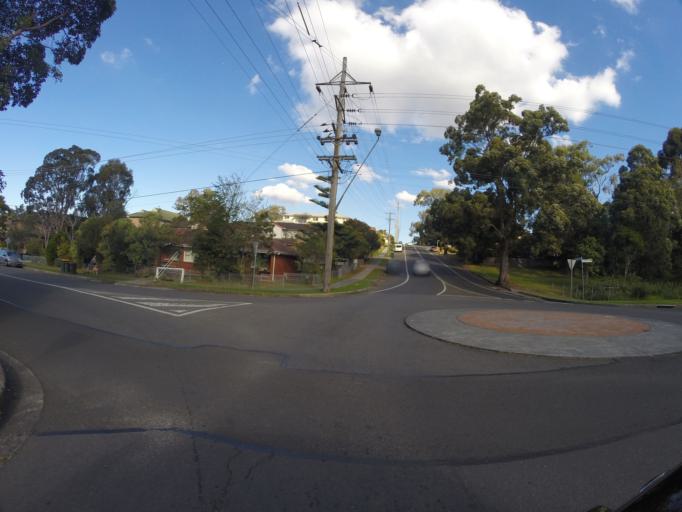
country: AU
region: New South Wales
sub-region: Wollongong
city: Keiraville
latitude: -34.4144
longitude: 150.8704
